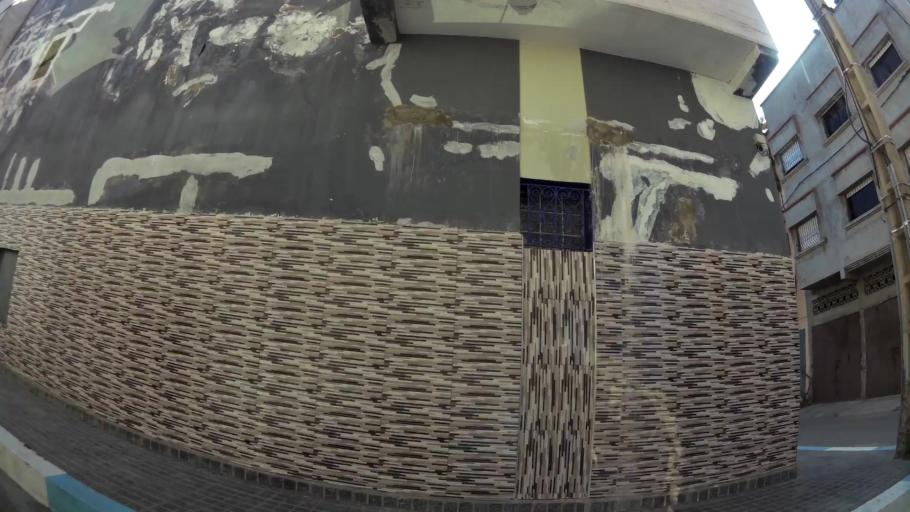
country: MA
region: Rabat-Sale-Zemmour-Zaer
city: Sale
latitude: 34.0710
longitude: -6.7959
